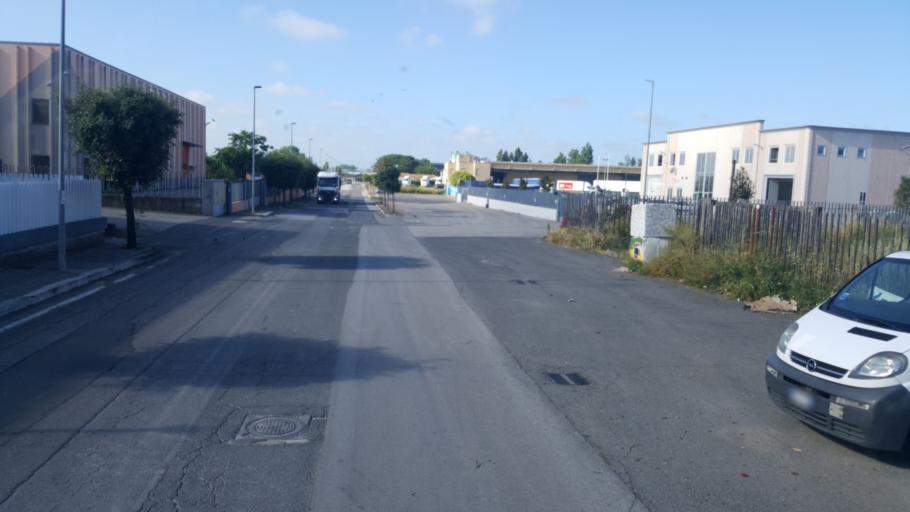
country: IT
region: Latium
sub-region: Provincia di Latina
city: Aprilia
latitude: 41.5738
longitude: 12.6466
